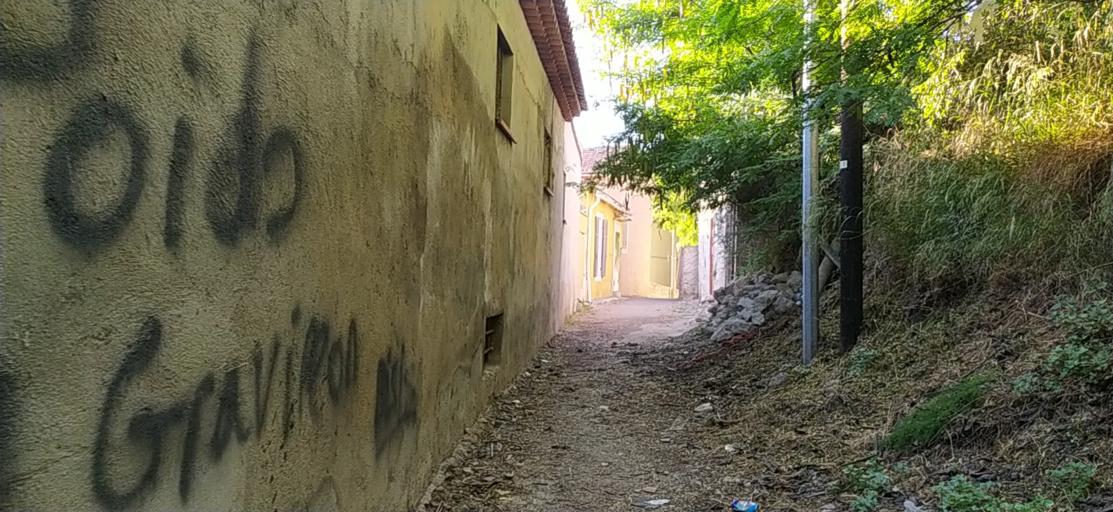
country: FR
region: Provence-Alpes-Cote d'Azur
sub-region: Departement des Bouches-du-Rhone
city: Marseille 14
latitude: 43.3329
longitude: 5.3570
